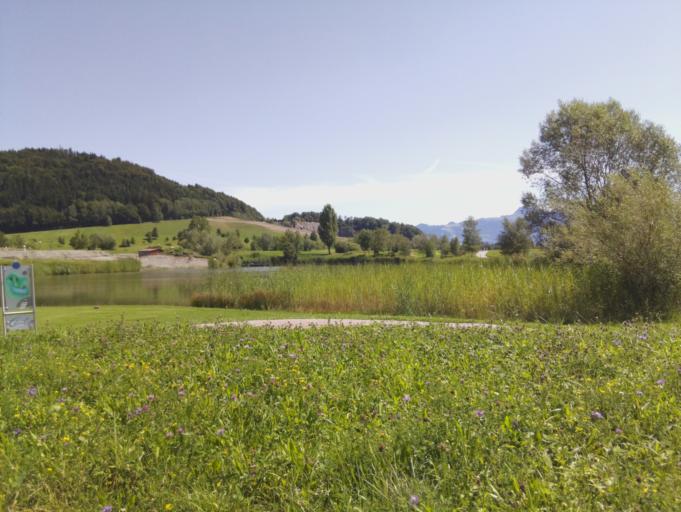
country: CH
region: Schwyz
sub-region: Bezirk March
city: Schubelbach
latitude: 47.1952
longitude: 8.8987
